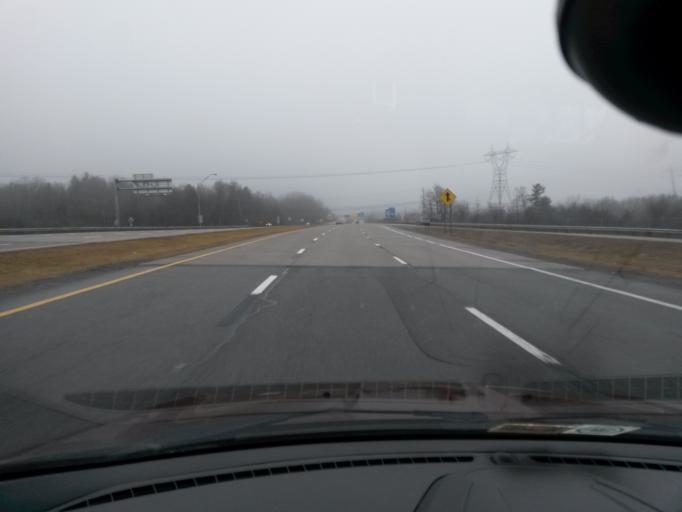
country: US
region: West Virginia
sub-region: Raleigh County
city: Daniels
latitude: 37.7668
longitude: -81.1254
